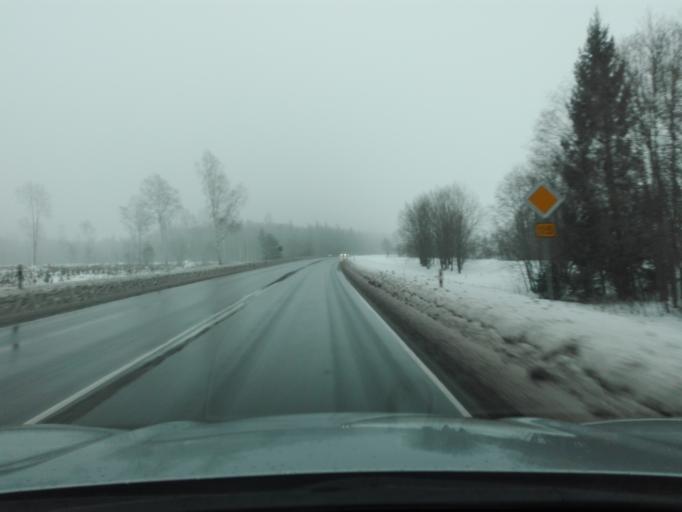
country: EE
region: Raplamaa
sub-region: Kohila vald
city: Kohila
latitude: 59.2322
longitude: 24.7726
